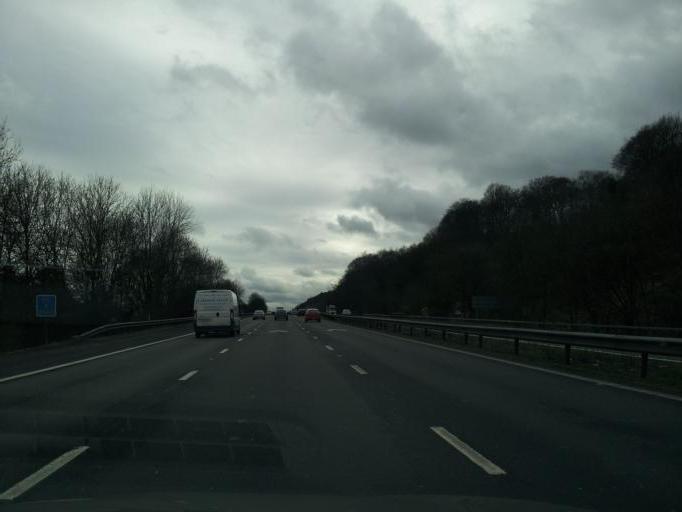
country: GB
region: England
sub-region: Staffordshire
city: Barlaston
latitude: 52.9481
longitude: -2.2175
